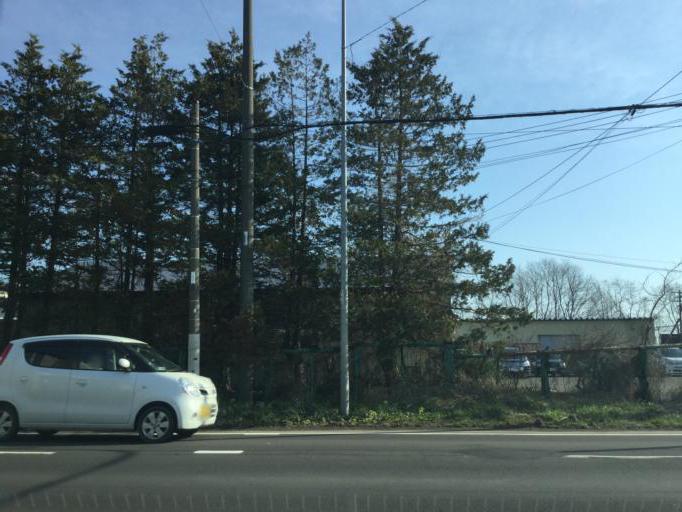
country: JP
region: Hokkaido
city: Ebetsu
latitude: 43.1199
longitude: 141.5462
